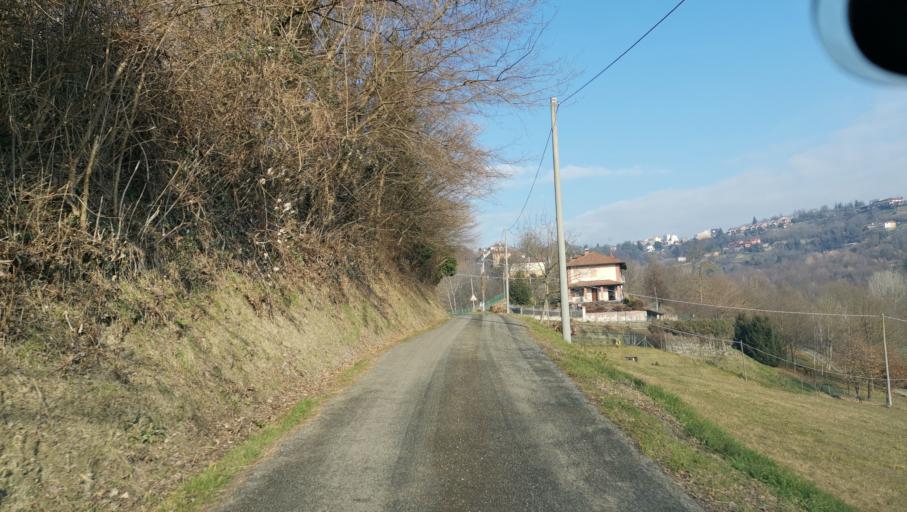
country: IT
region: Piedmont
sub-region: Provincia di Torino
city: San Raffaele Cimena
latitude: 45.1428
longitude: 7.8588
